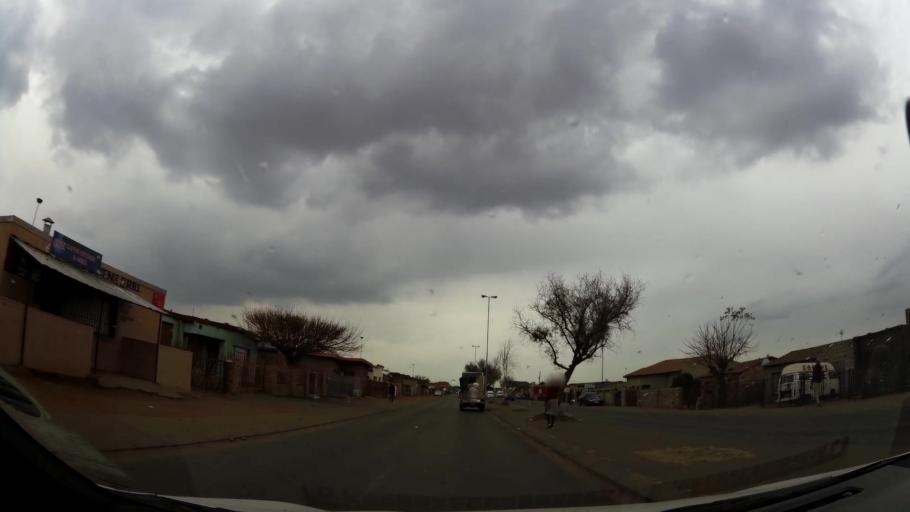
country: ZA
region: Gauteng
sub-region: Ekurhuleni Metropolitan Municipality
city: Germiston
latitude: -26.3510
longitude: 28.1498
